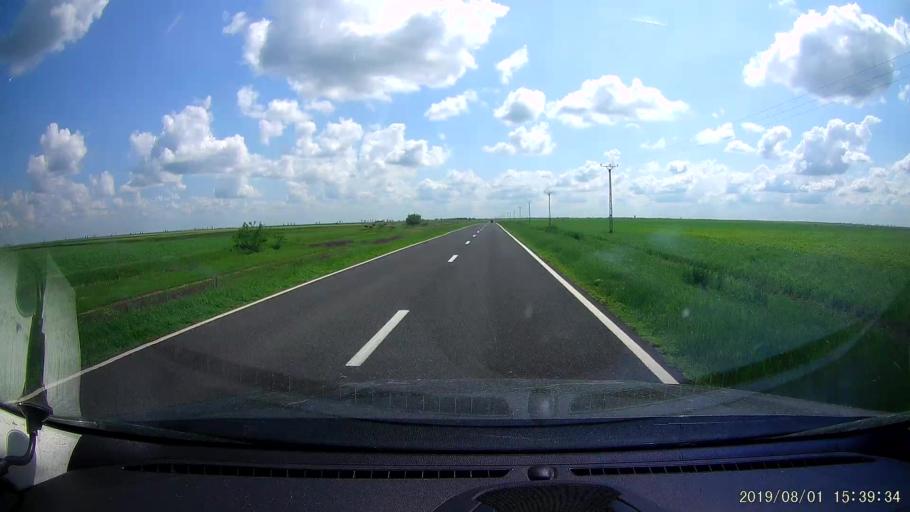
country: RO
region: Braila
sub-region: Comuna Baraganul
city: Baraganul
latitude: 44.8544
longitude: 27.5569
